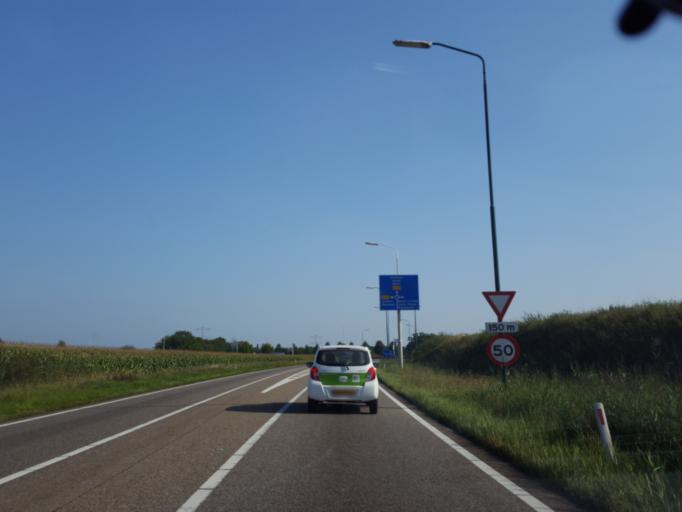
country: NL
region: North Brabant
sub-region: Gemeente Laarbeek
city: Aarle-Rixtel
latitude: 51.5400
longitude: 5.6564
